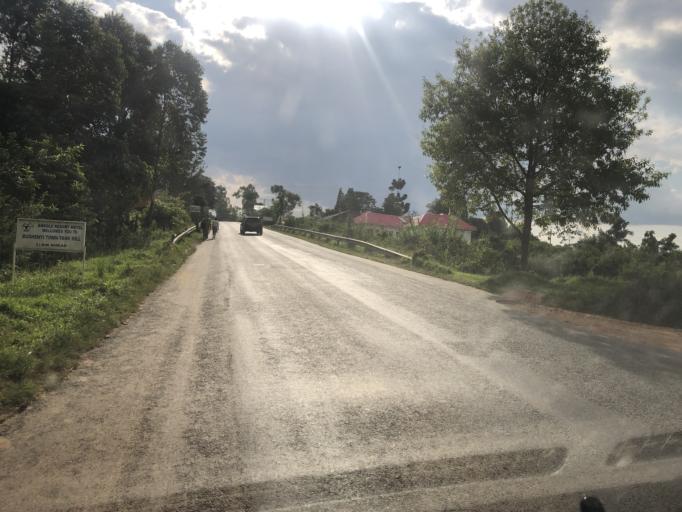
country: UG
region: Western Region
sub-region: Bushenyi District
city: Bushenyi
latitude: -0.5427
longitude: 30.2031
